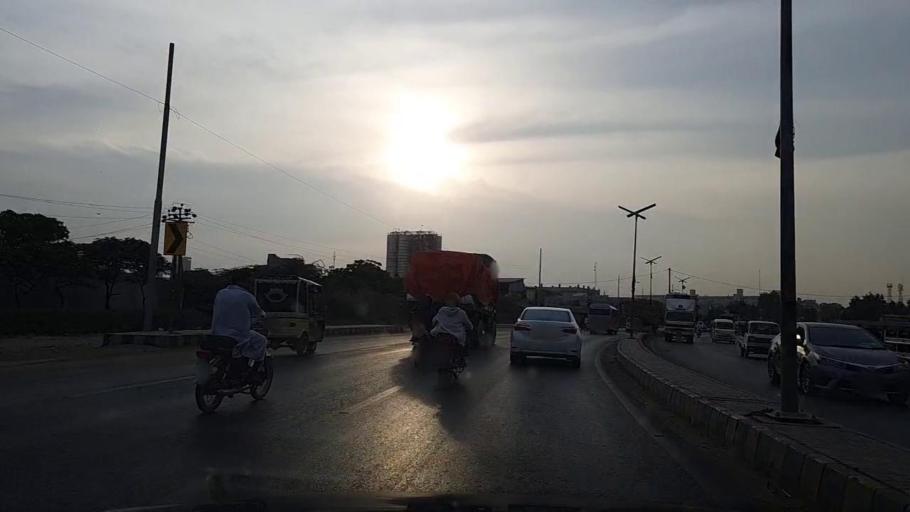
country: PK
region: Sindh
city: Malir Cantonment
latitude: 24.8533
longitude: 67.2495
